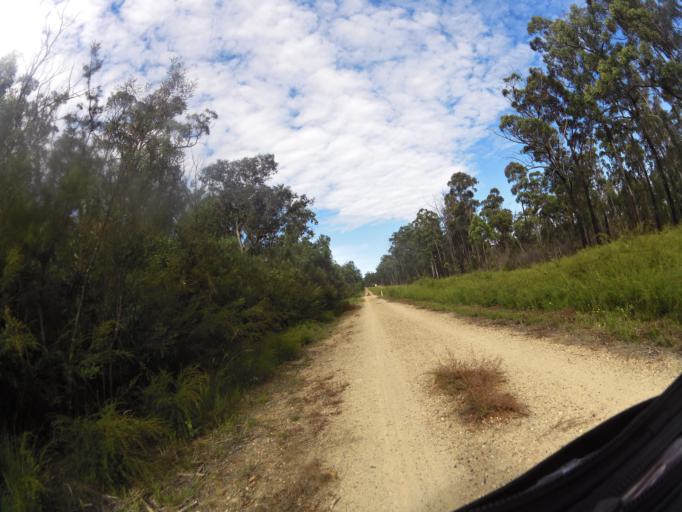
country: AU
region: Victoria
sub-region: East Gippsland
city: Lakes Entrance
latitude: -37.7471
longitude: 148.2301
